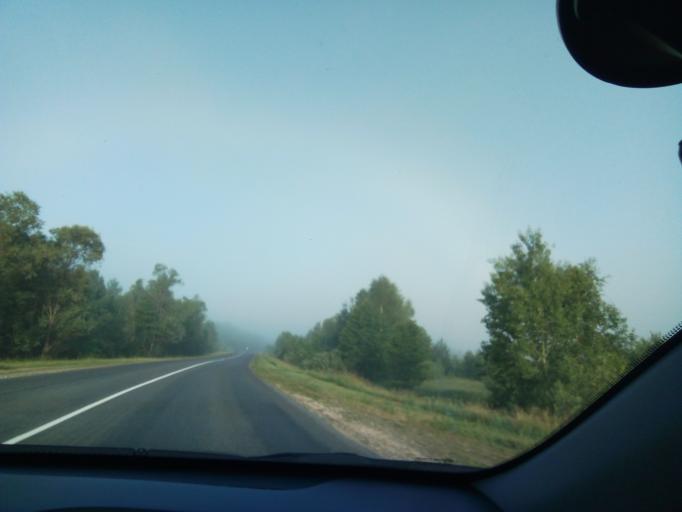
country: RU
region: Nizjnij Novgorod
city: Voznesenskoye
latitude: 54.8634
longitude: 42.9430
